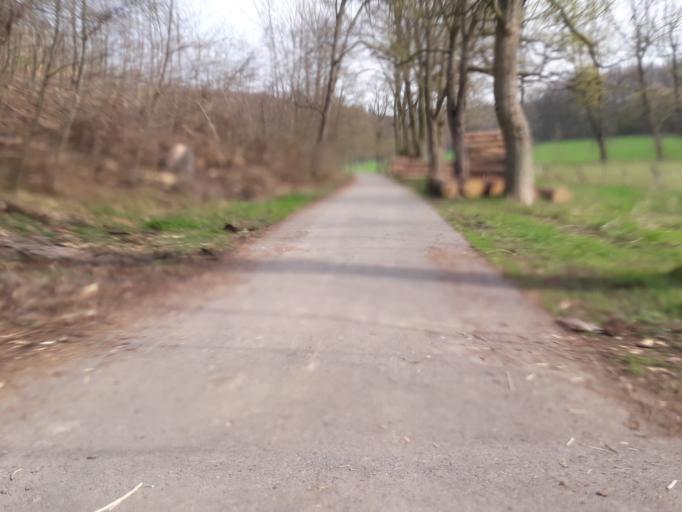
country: DE
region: North Rhine-Westphalia
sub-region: Regierungsbezirk Detmold
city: Paderborn
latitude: 51.6854
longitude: 8.7853
